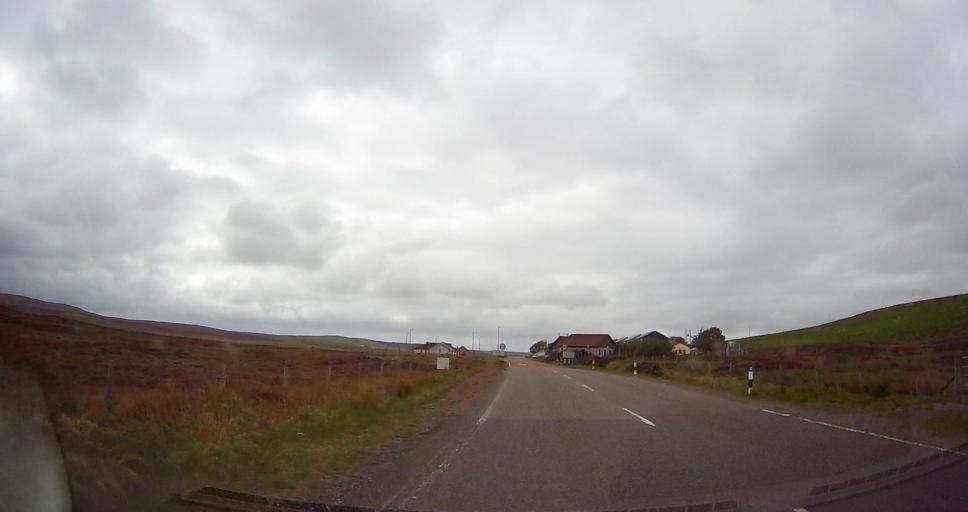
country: GB
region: Scotland
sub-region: Shetland Islands
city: Lerwick
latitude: 60.2528
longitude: -1.3939
